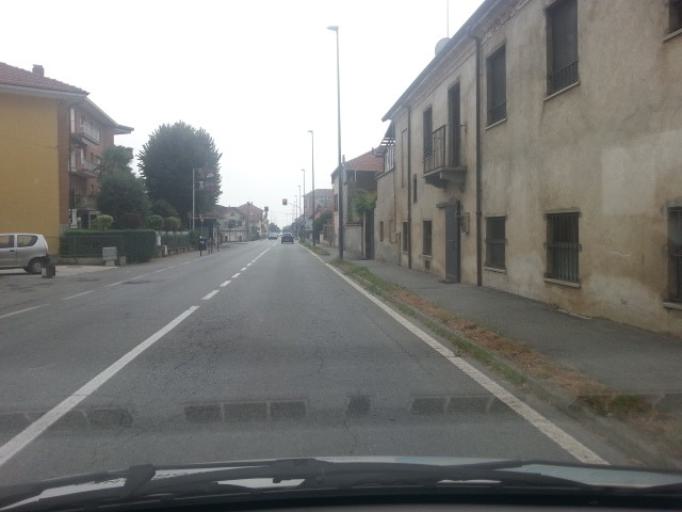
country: IT
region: Piedmont
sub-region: Provincia di Torino
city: Piossasco
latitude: 44.9933
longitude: 7.4678
